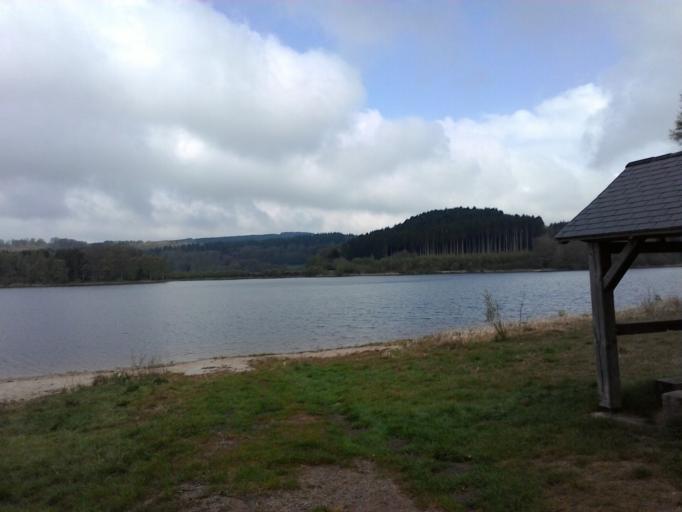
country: FR
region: Bourgogne
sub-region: Departement de la Cote-d'Or
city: Saulieu
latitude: 47.2492
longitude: 4.1946
